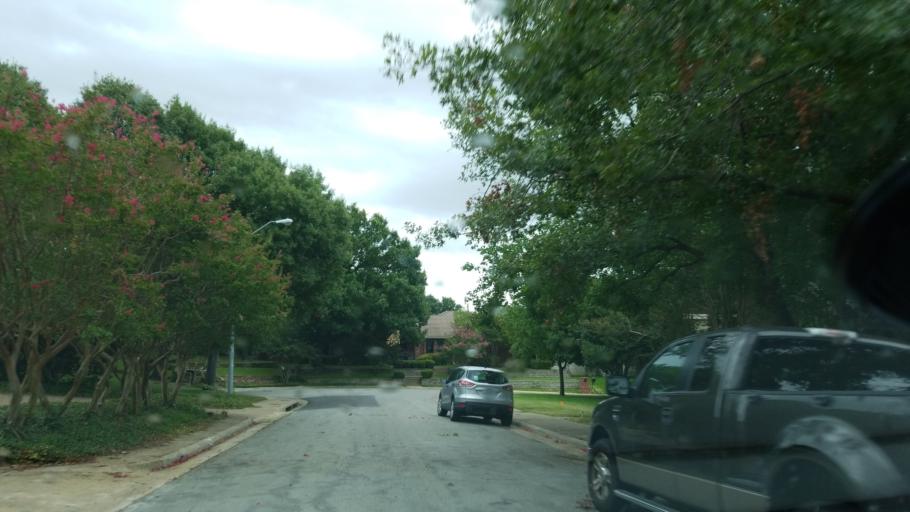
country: US
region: Texas
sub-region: Dallas County
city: Richardson
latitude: 32.8960
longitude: -96.7368
